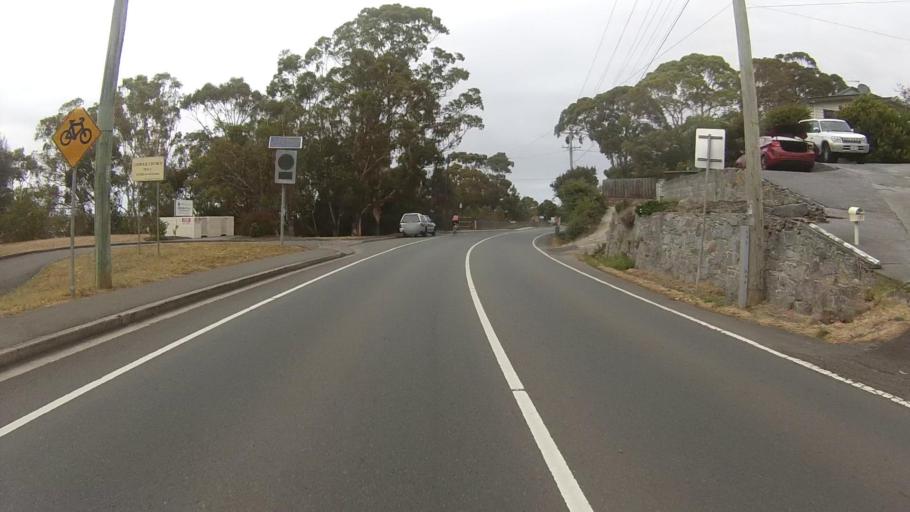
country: AU
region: Tasmania
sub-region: Kingborough
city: Taroona
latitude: -42.9417
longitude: 147.3526
